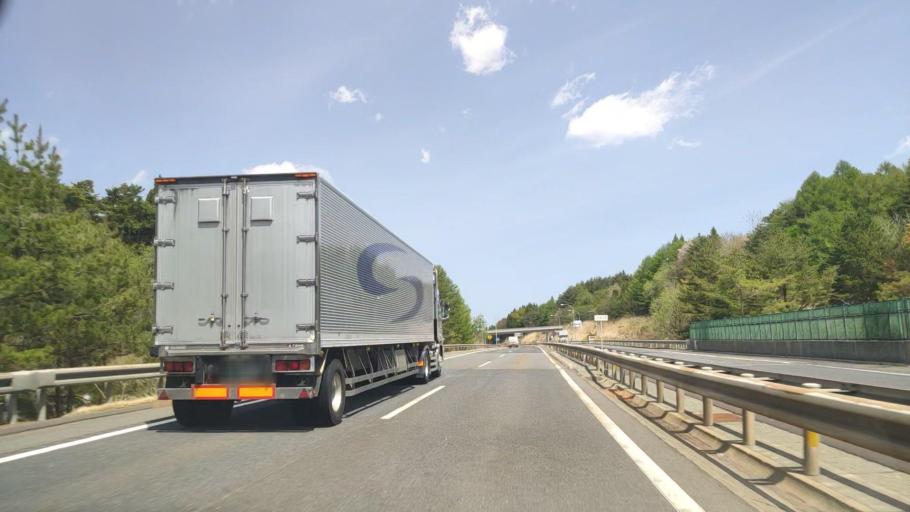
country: JP
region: Aomori
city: Hachinohe
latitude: 40.4069
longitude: 141.4436
